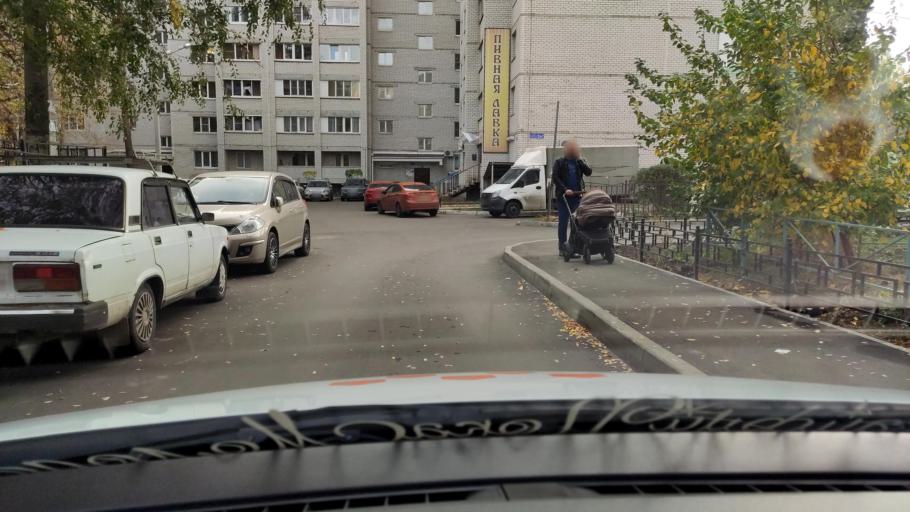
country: RU
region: Voronezj
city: Podgornoye
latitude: 51.6864
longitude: 39.1284
